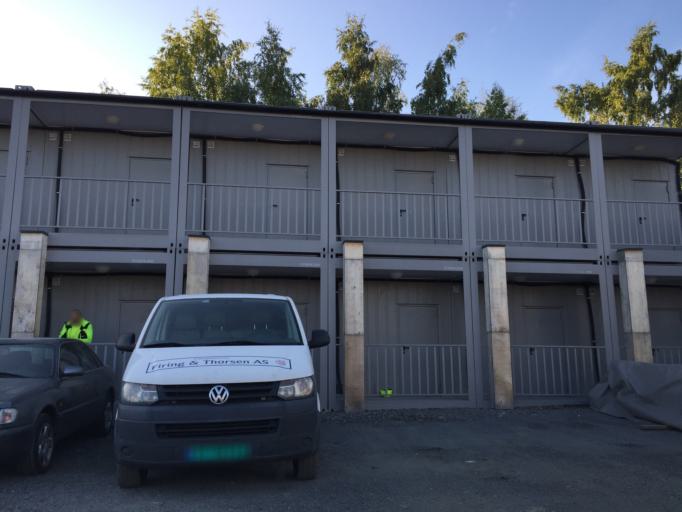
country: NO
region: Akershus
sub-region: Baerum
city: Lysaker
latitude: 59.9007
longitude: 10.6126
